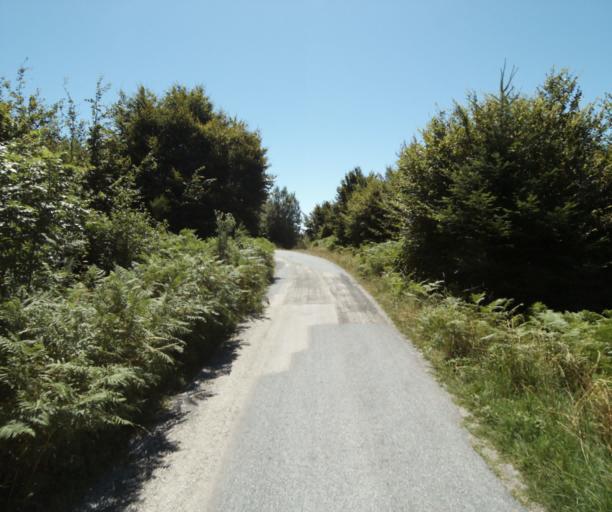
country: FR
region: Languedoc-Roussillon
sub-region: Departement de l'Aude
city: Cuxac-Cabardes
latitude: 43.4071
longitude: 2.2013
